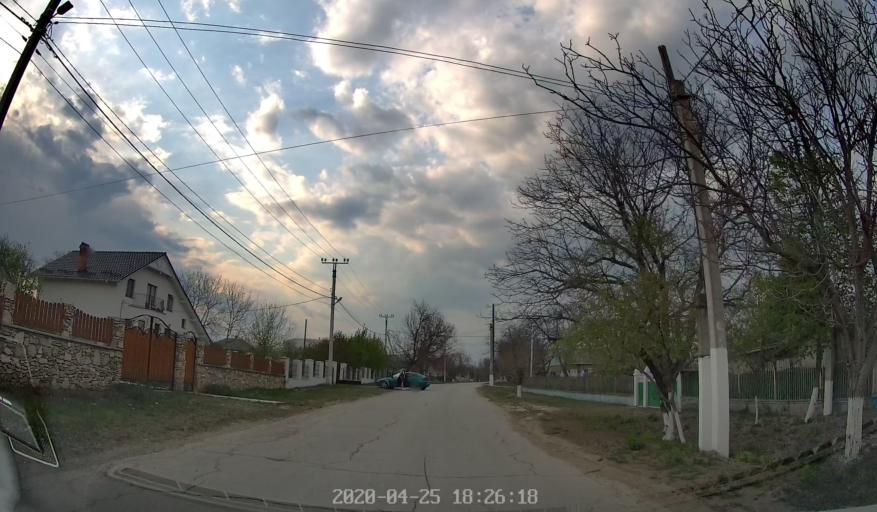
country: MD
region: Criuleni
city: Criuleni
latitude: 47.1661
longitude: 29.1268
